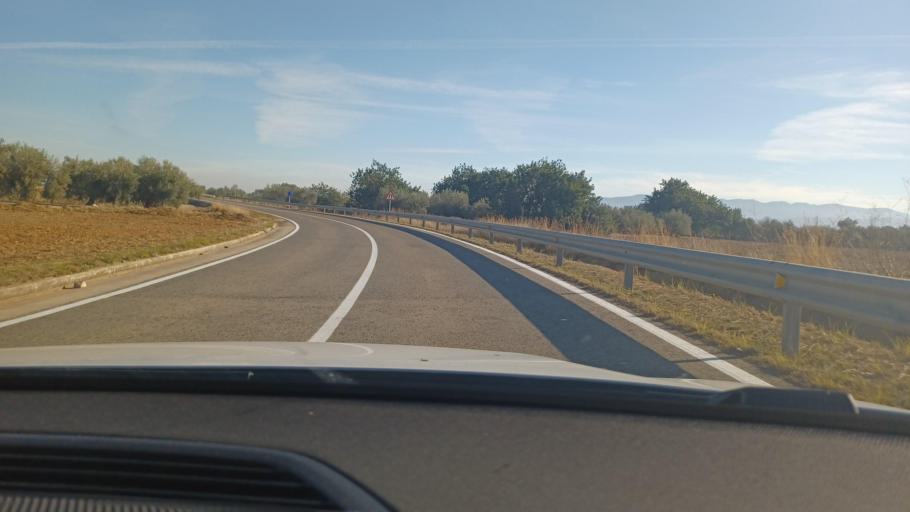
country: ES
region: Catalonia
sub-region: Provincia de Tarragona
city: Santa Barbara
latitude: 40.7196
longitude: 0.4477
